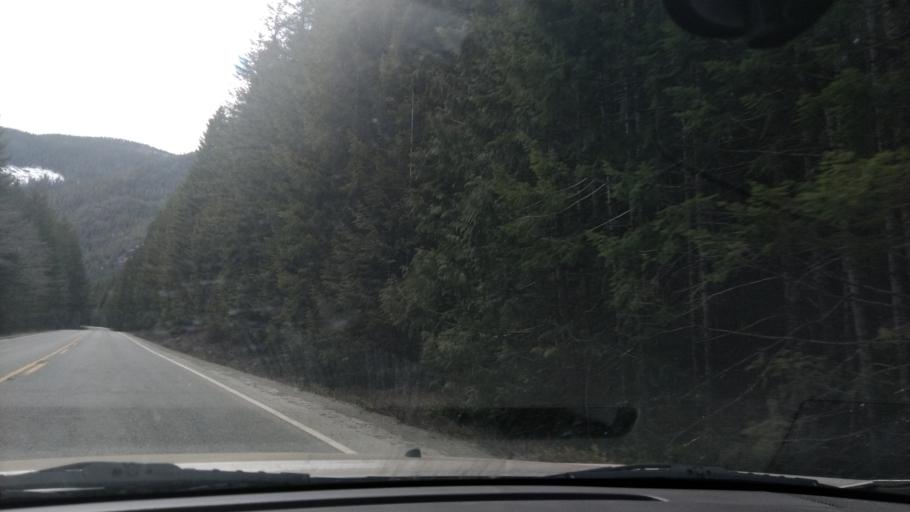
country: CA
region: British Columbia
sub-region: Regional District of Alberni-Clayoquot
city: Tofino
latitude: 49.8309
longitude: -125.9702
